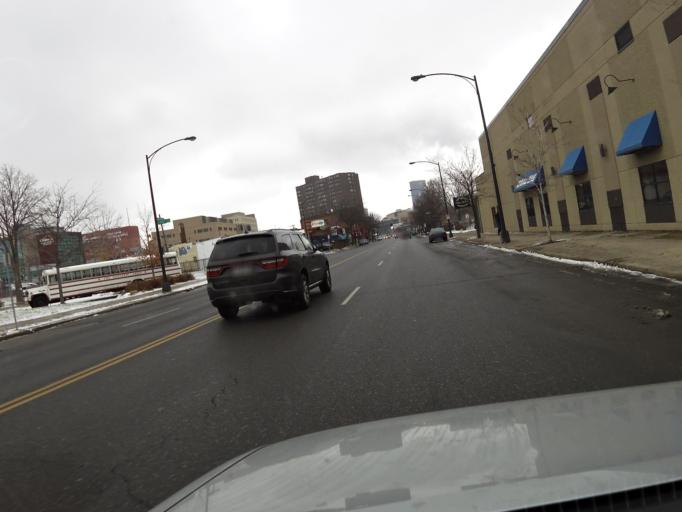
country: US
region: Minnesota
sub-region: Ramsey County
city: Saint Paul
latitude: 44.9397
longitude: -93.1091
